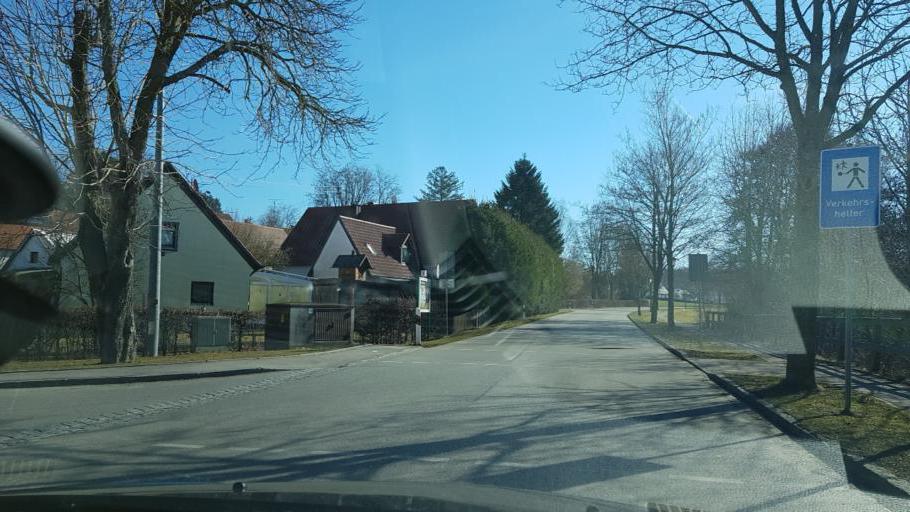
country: DE
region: Bavaria
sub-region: Upper Bavaria
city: Oberschweinbach
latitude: 48.2380
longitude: 11.1561
